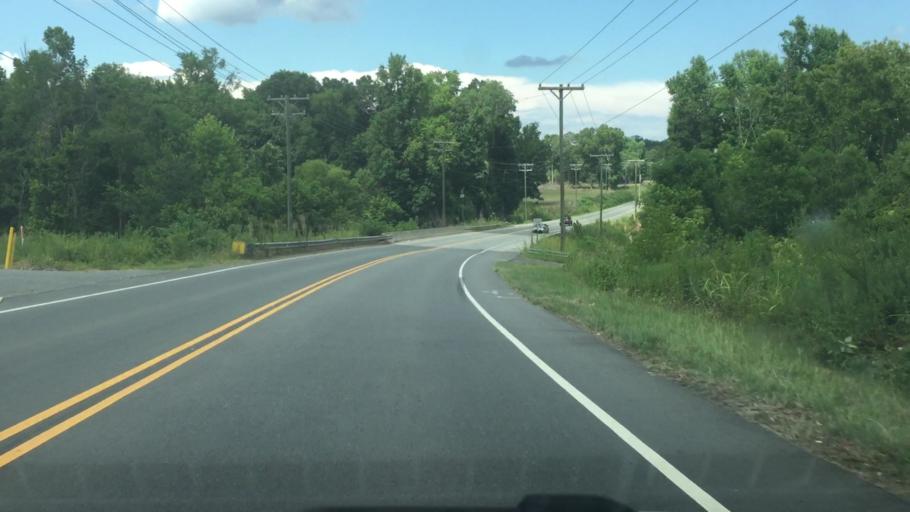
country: US
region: North Carolina
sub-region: Mecklenburg County
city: Huntersville
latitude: 35.4134
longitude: -80.7527
